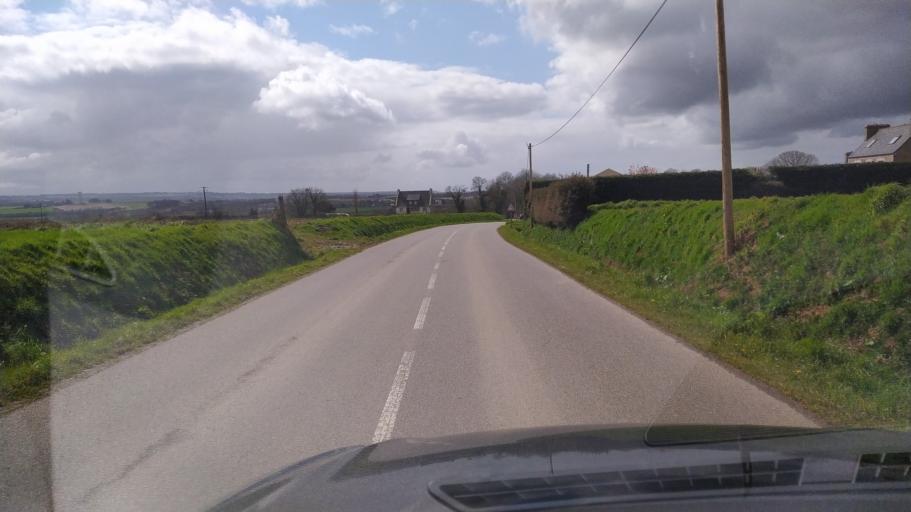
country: FR
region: Brittany
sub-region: Departement du Finistere
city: Bodilis
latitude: 48.5265
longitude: -4.1220
